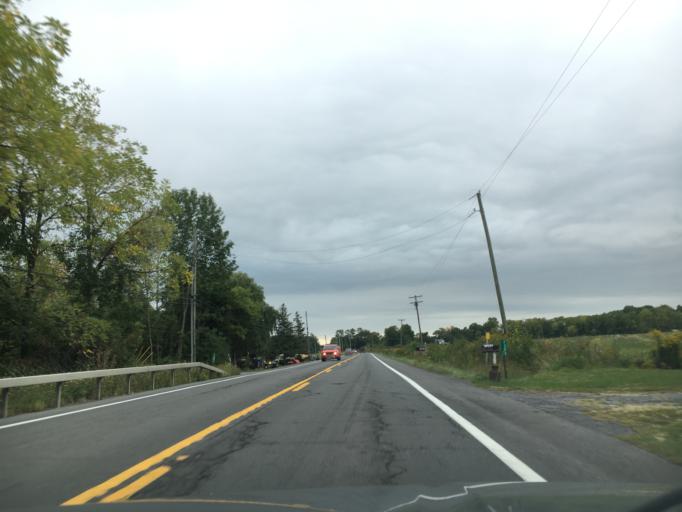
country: US
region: New York
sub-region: Tompkins County
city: Trumansburg
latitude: 42.6675
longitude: -76.7289
